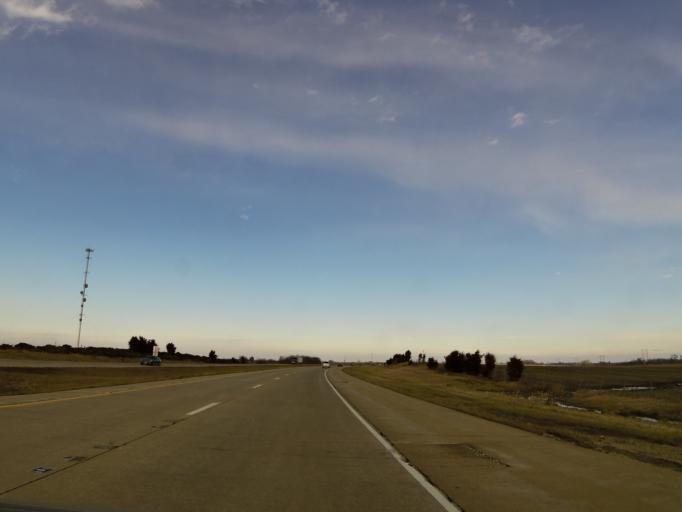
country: US
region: Illinois
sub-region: LaSalle County
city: Oglesby
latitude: 41.2541
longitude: -89.0794
